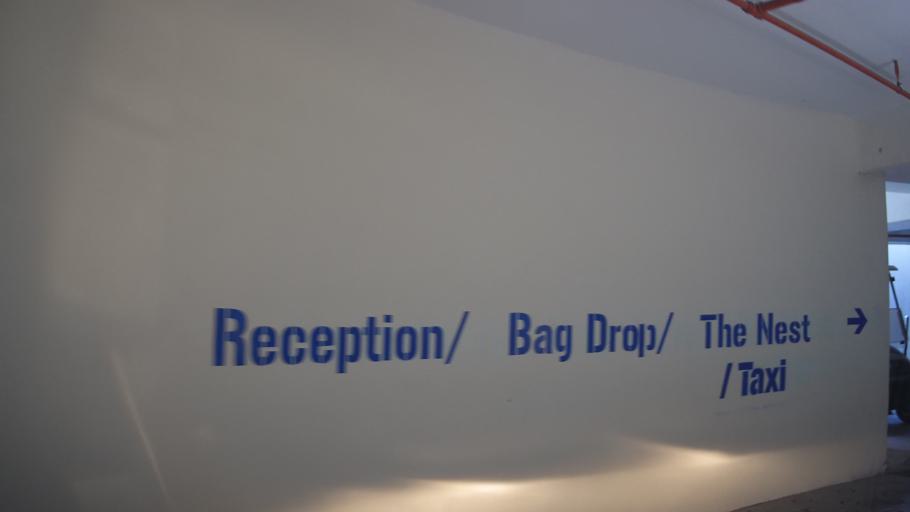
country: SG
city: Singapore
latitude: 1.3213
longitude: 103.9612
